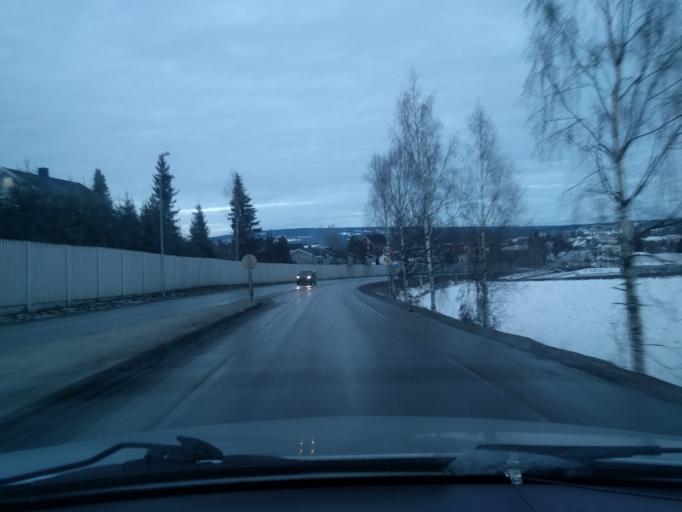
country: NO
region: Hedmark
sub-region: Hamar
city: Hamar
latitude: 60.8103
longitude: 11.0900
